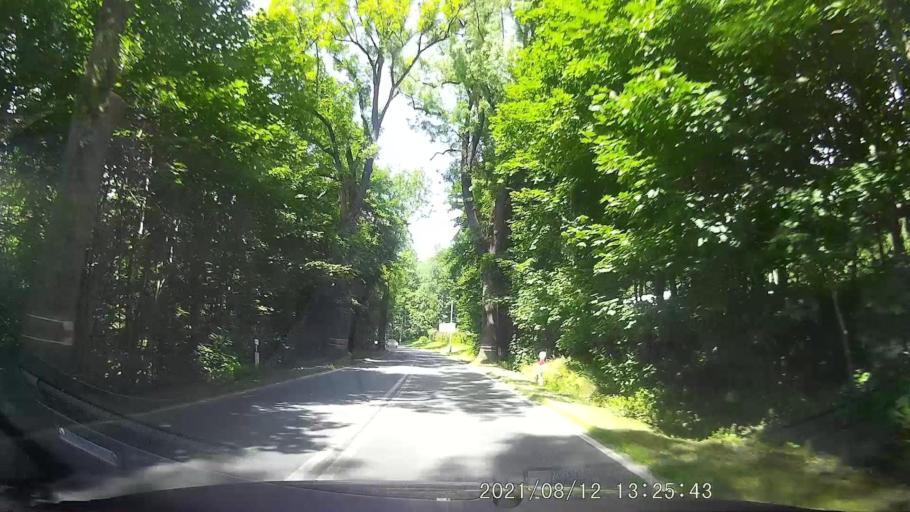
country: PL
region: Lower Silesian Voivodeship
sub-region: Powiat klodzki
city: Ladek-Zdroj
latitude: 50.3236
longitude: 16.8864
